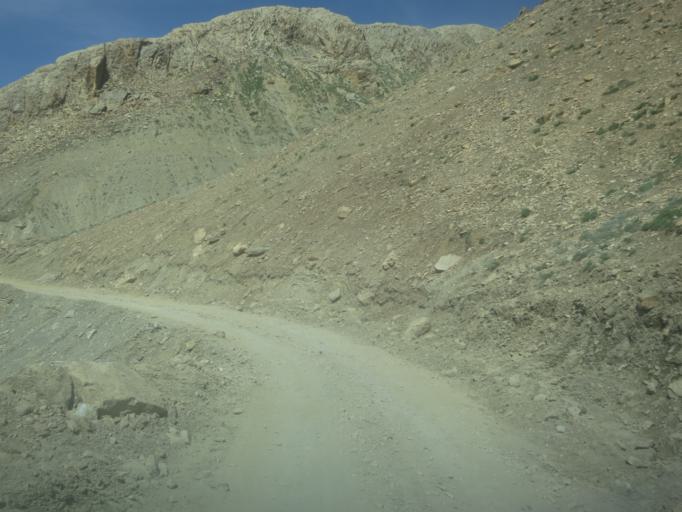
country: IN
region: Himachal Pradesh
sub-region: Kulu
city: Manali
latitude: 32.4289
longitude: 77.6740
